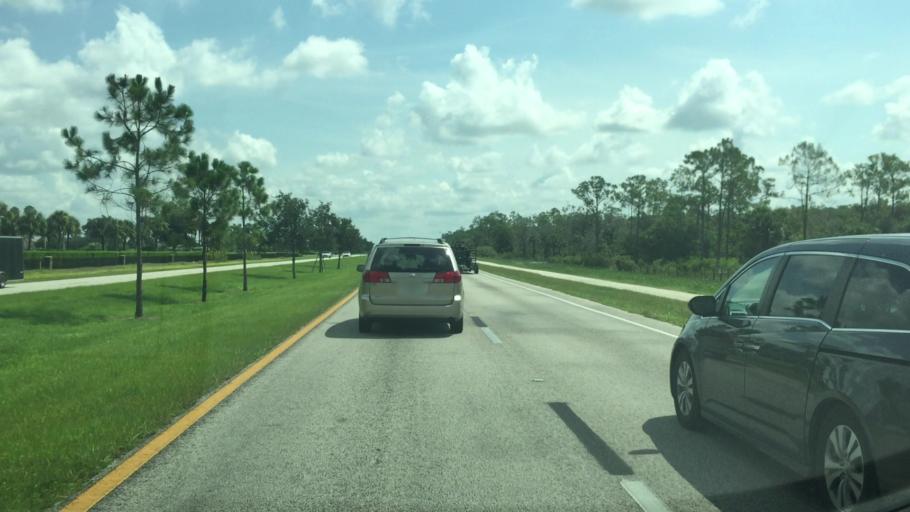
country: US
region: Florida
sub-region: Lee County
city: Fort Myers
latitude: 26.5842
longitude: -81.8207
